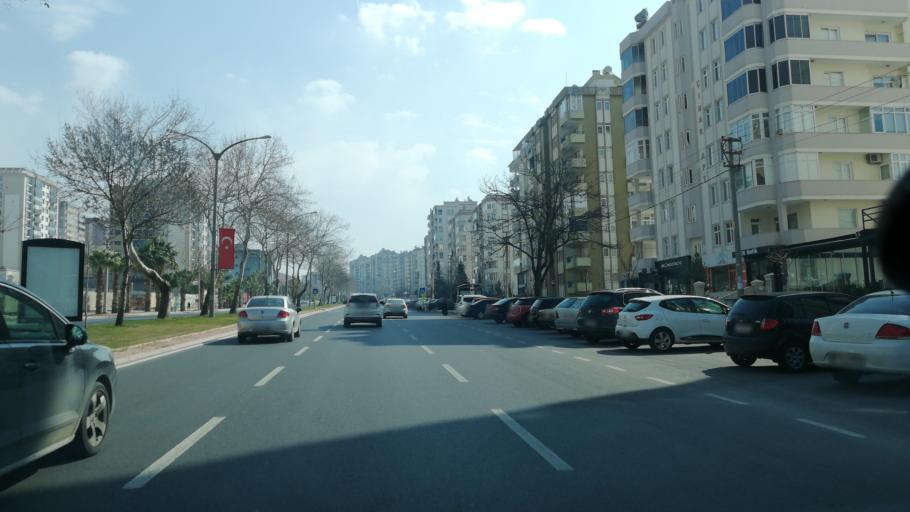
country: TR
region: Kahramanmaras
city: Kahramanmaras
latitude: 37.5902
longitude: 36.8730
